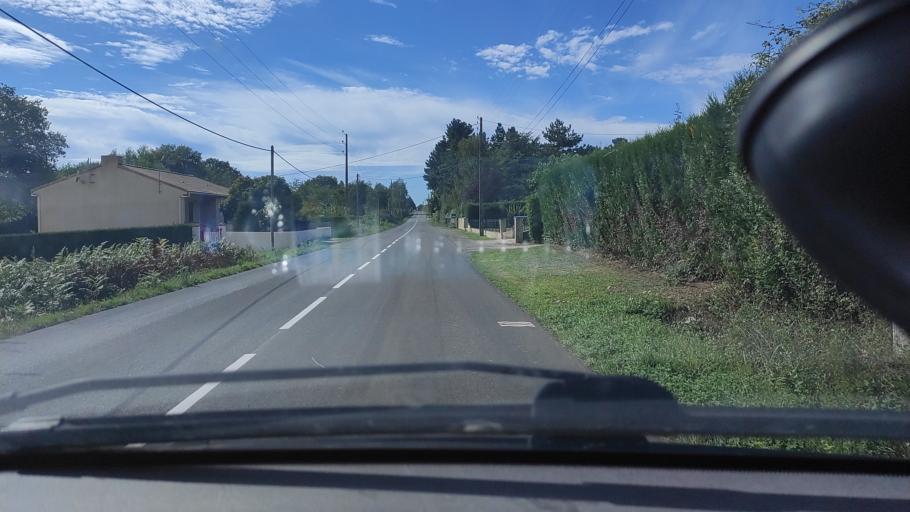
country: FR
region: Pays de la Loire
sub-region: Departement de la Vendee
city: Saint-Vincent-sur-Graon
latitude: 46.5455
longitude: -1.4051
